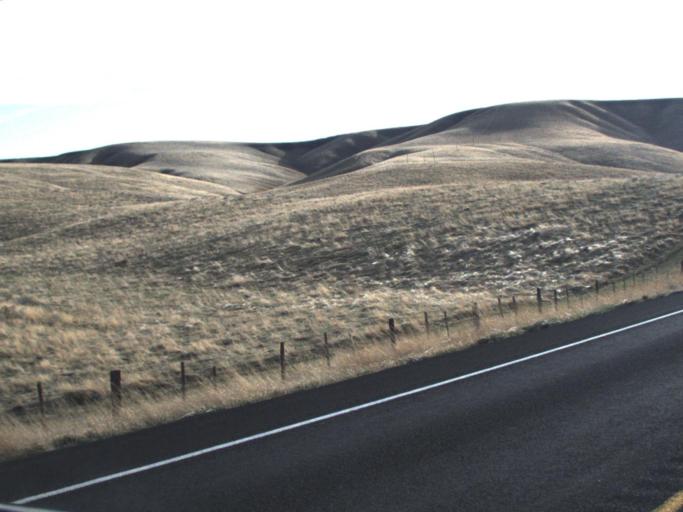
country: US
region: Washington
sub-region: Columbia County
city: Dayton
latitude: 46.5190
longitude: -117.9378
